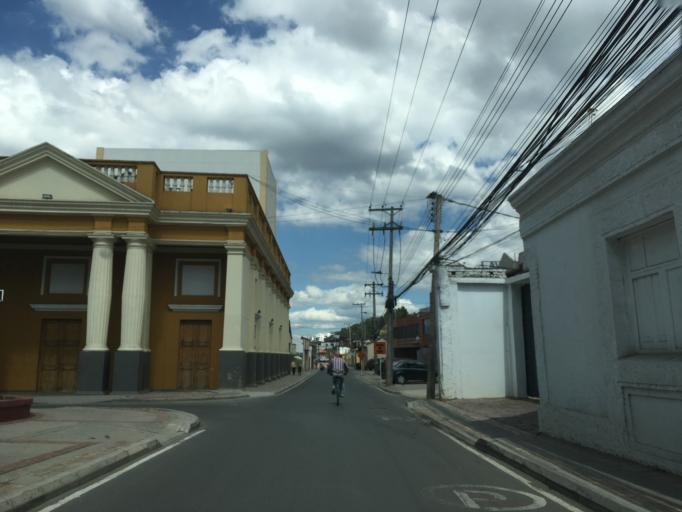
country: CO
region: Boyaca
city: Sogamoso
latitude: 5.7142
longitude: -72.9260
